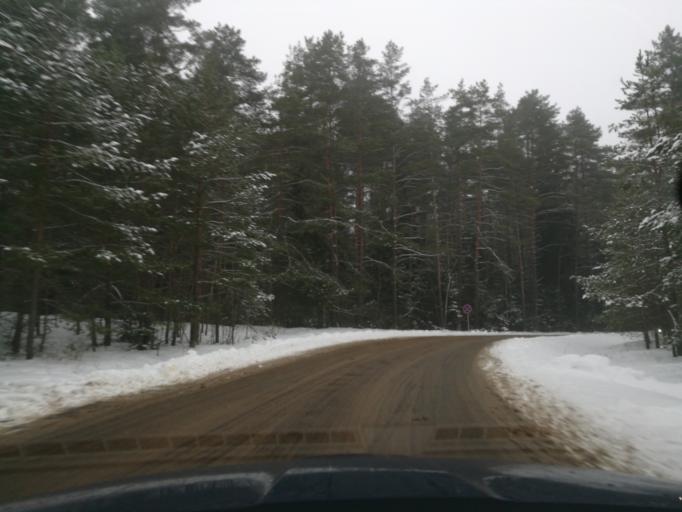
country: LT
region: Utenos apskritis
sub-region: Anyksciai
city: Anyksciai
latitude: 55.4670
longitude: 25.0489
